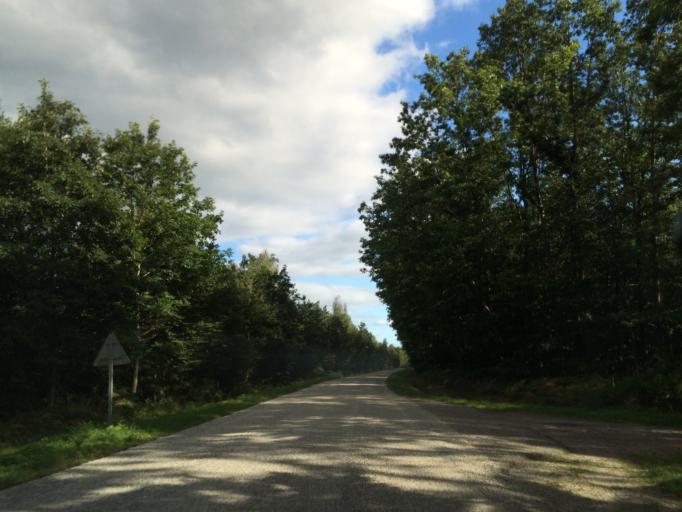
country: FR
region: Alsace
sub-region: Departement du Bas-Rhin
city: Betschdorf
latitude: 48.8760
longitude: 7.9289
